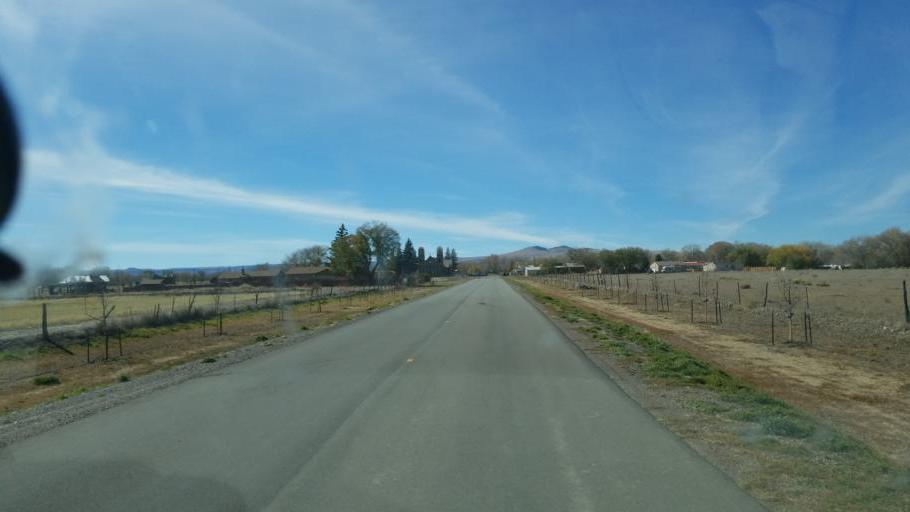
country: US
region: Colorado
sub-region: Conejos County
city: Conejos
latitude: 37.0892
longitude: -106.0158
